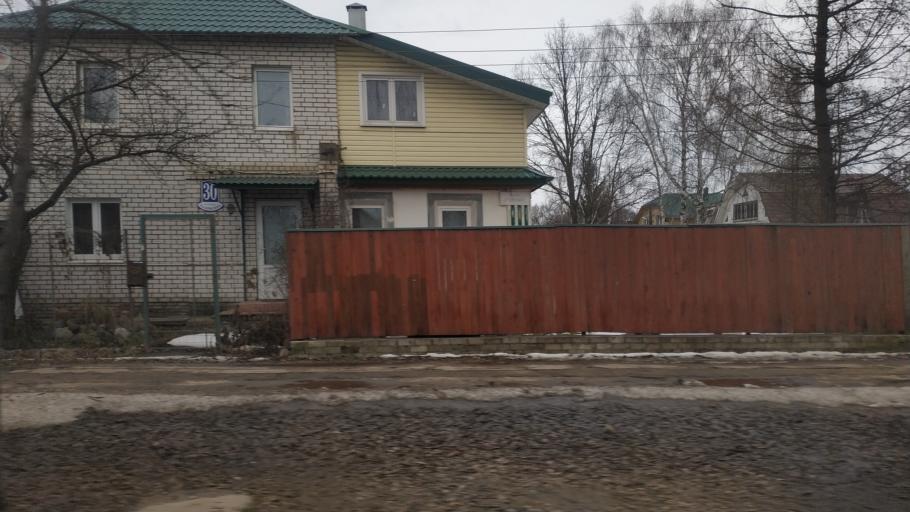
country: RU
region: Tverskaya
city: Tver
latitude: 56.8807
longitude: 35.8876
